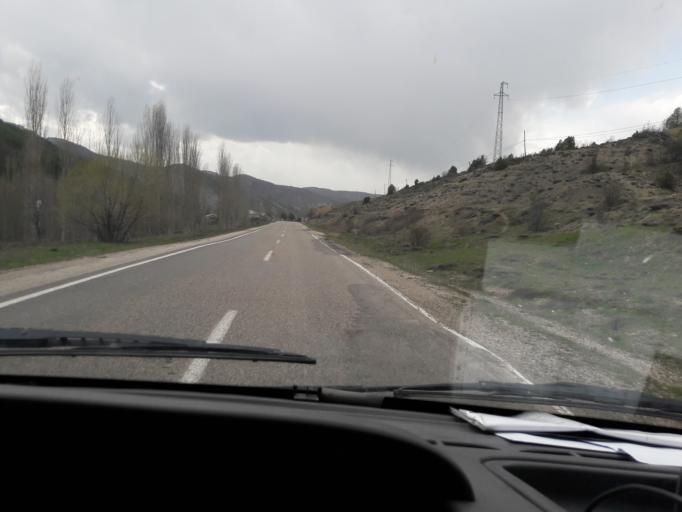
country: TR
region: Giresun
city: Alucra
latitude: 40.2744
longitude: 38.8522
